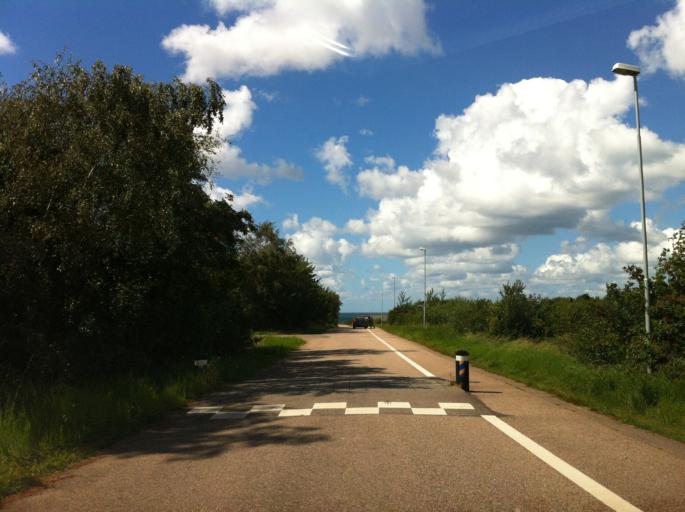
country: SE
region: Skane
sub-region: Bastads Kommun
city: Forslov
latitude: 56.3091
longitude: 12.8136
